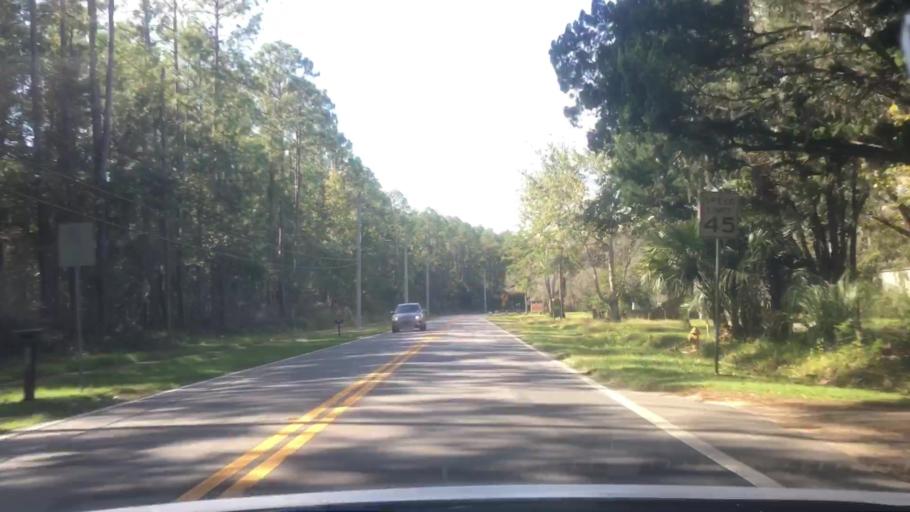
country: US
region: Florida
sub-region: Nassau County
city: Yulee
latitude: 30.5019
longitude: -81.5836
